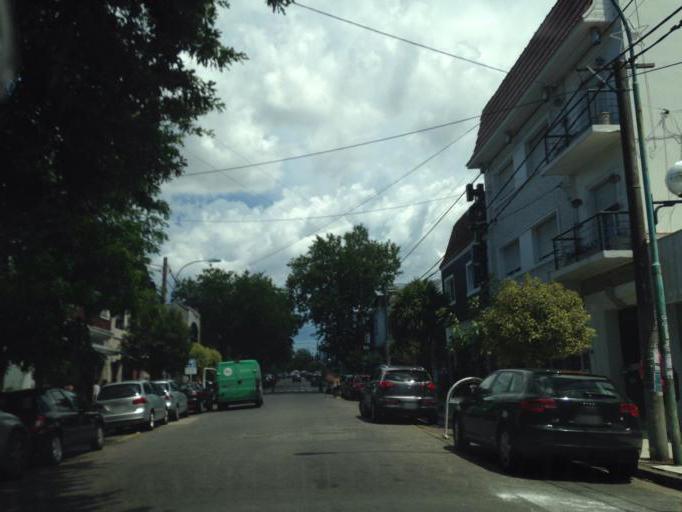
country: AR
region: Buenos Aires
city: Mar del Plata
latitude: -38.0167
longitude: -57.5424
